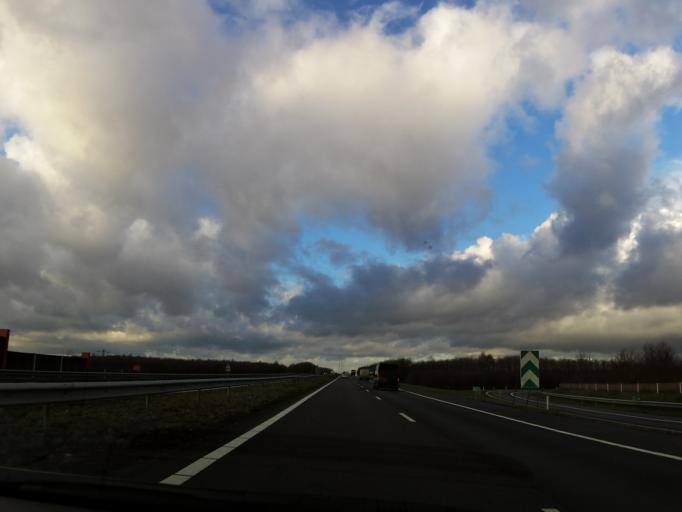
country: NL
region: North Brabant
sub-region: Gemeente Sint Anthonis
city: Sint Anthonis
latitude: 51.6636
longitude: 5.9041
